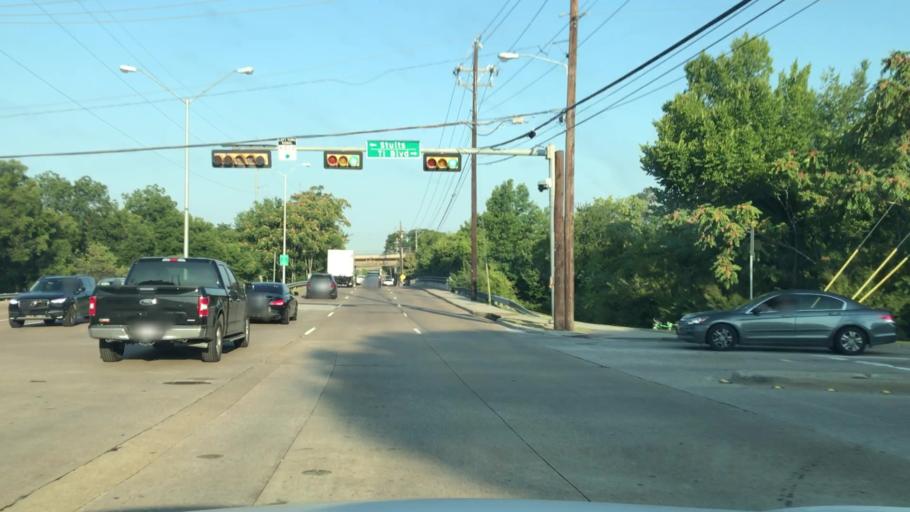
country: US
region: Texas
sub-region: Dallas County
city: Richardson
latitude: 32.9093
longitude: -96.7585
